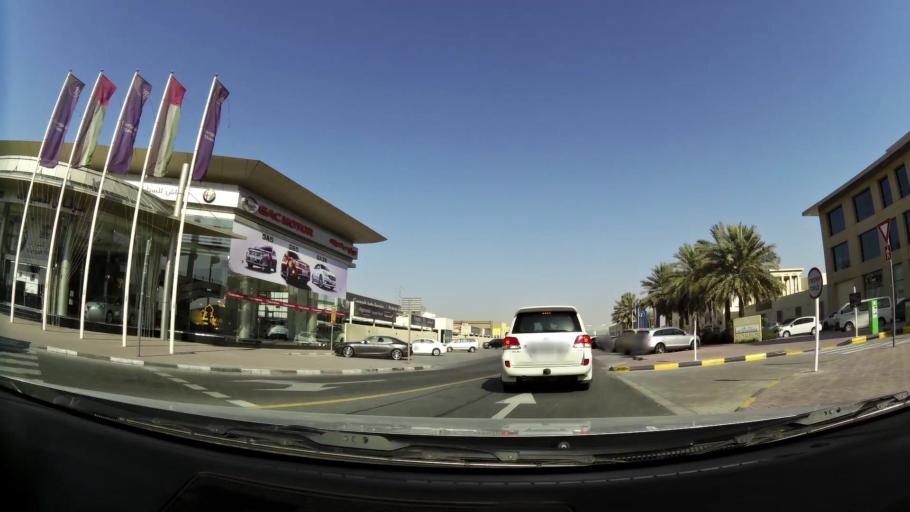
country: AE
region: Dubai
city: Dubai
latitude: 25.1272
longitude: 55.2092
